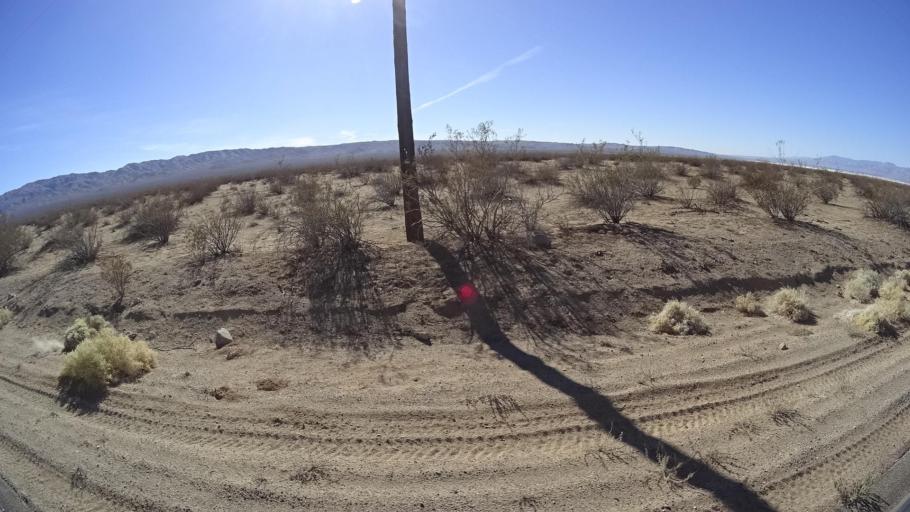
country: US
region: California
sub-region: Kern County
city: Ridgecrest
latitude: 35.3889
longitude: -117.7638
